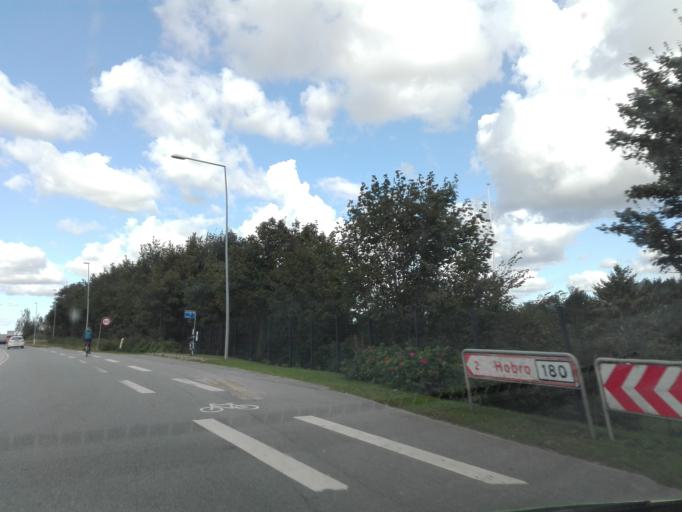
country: DK
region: North Denmark
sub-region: Mariagerfjord Kommune
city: Hobro
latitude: 56.6206
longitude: 9.8067
